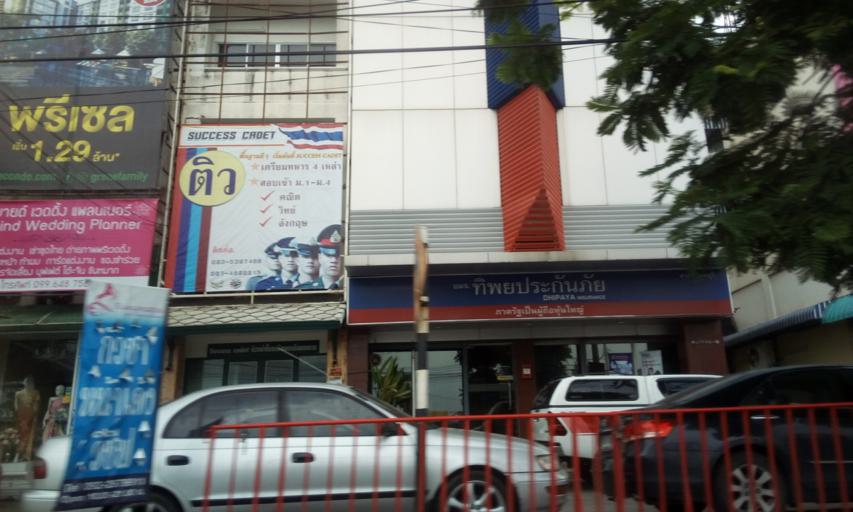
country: TH
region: Bangkok
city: Don Mueang
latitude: 13.9383
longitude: 100.5542
